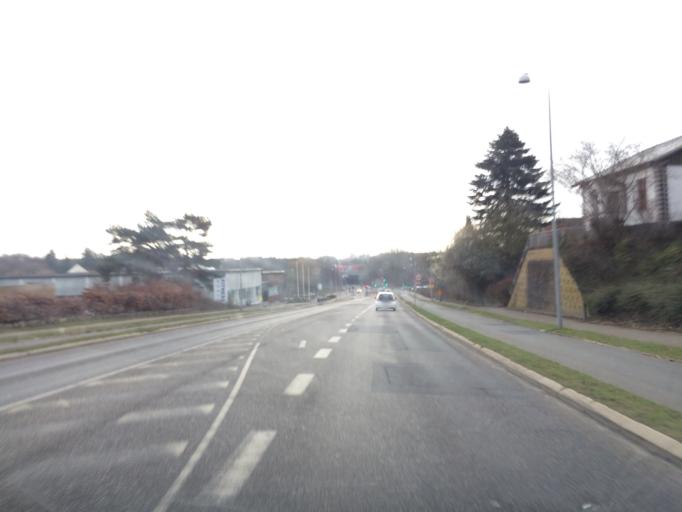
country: DK
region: South Denmark
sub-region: Fredericia Kommune
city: Fredericia
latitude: 55.5693
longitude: 9.7329
